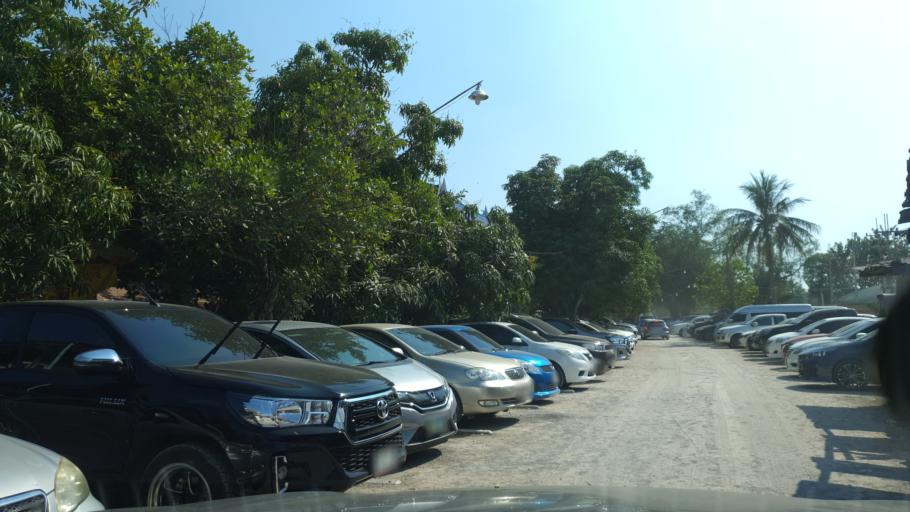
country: TH
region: Samut Songkhram
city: Amphawa
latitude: 13.4242
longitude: 99.9538
